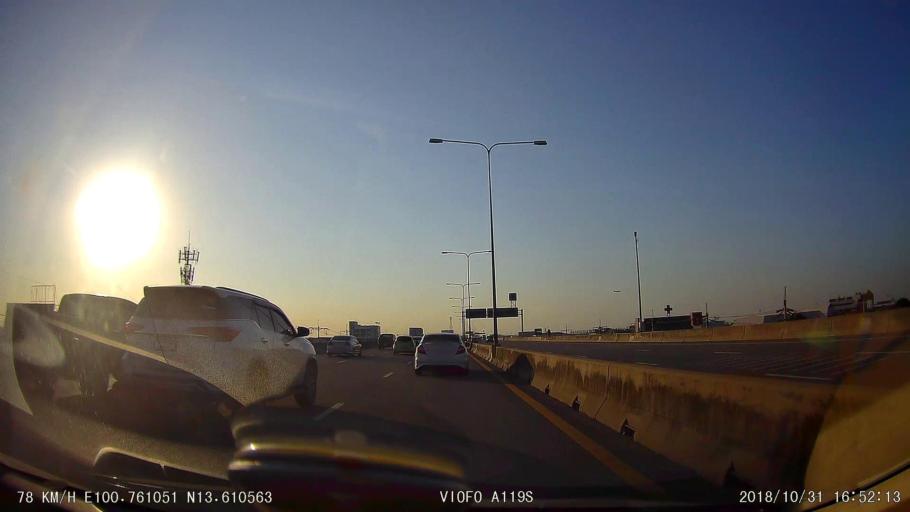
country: TH
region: Samut Prakan
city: Bang Bo District
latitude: 13.6107
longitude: 100.7609
